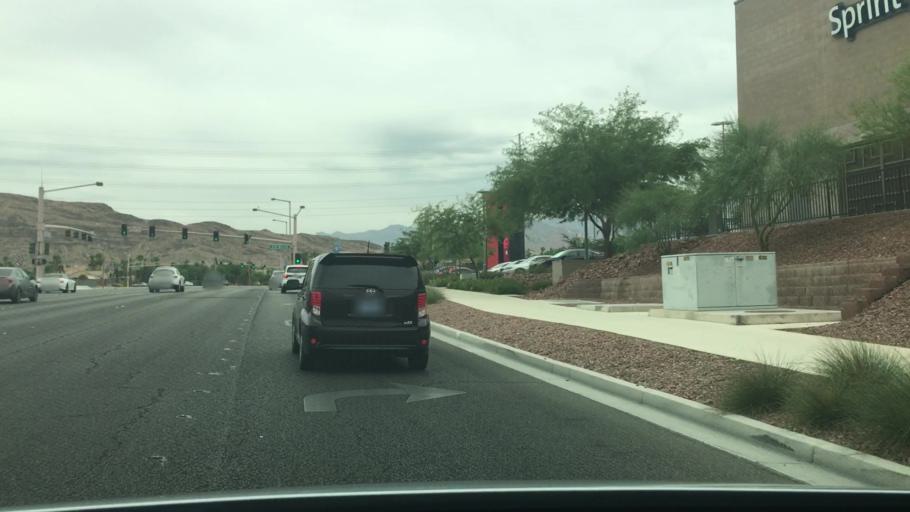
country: US
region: Nevada
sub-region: Clark County
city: Summerlin South
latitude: 36.1446
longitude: -115.3349
